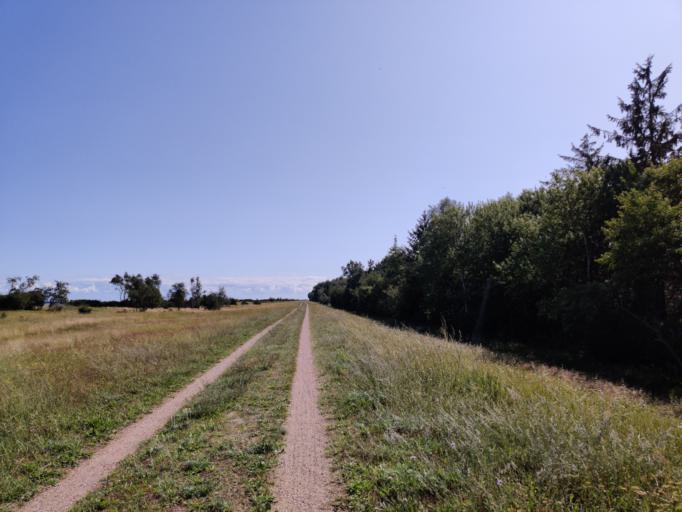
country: DK
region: Zealand
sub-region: Guldborgsund Kommune
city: Nykobing Falster
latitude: 54.6157
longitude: 11.9641
